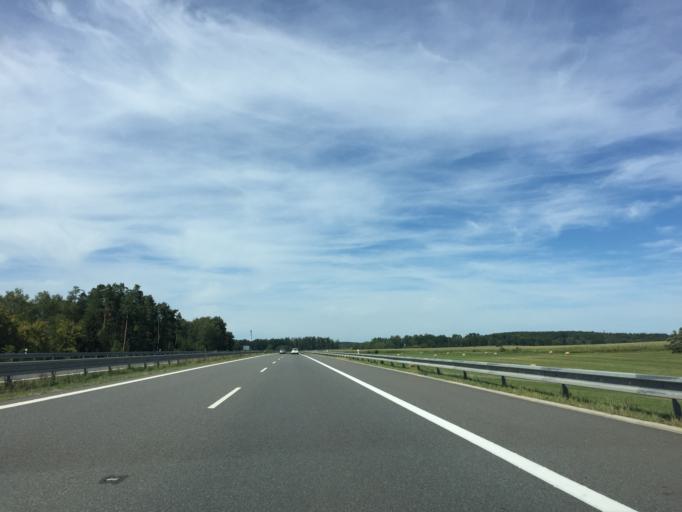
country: CZ
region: Jihocesky
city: Sobeslav
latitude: 49.2316
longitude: 14.7279
